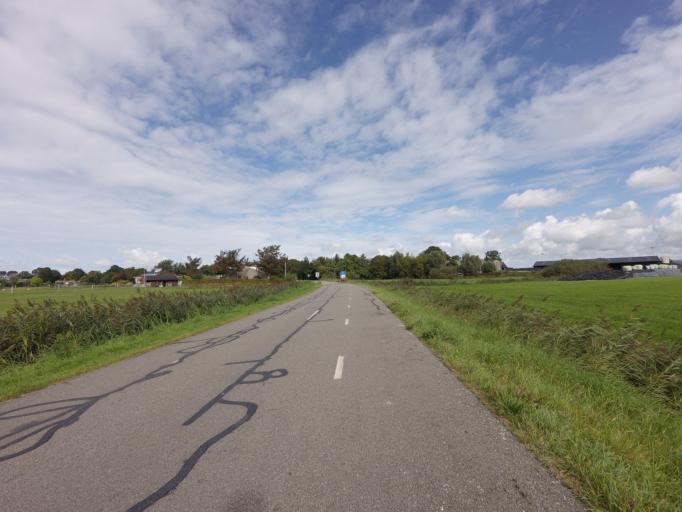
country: NL
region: Friesland
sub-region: Sudwest Fryslan
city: Makkum
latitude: 53.0815
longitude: 5.4264
